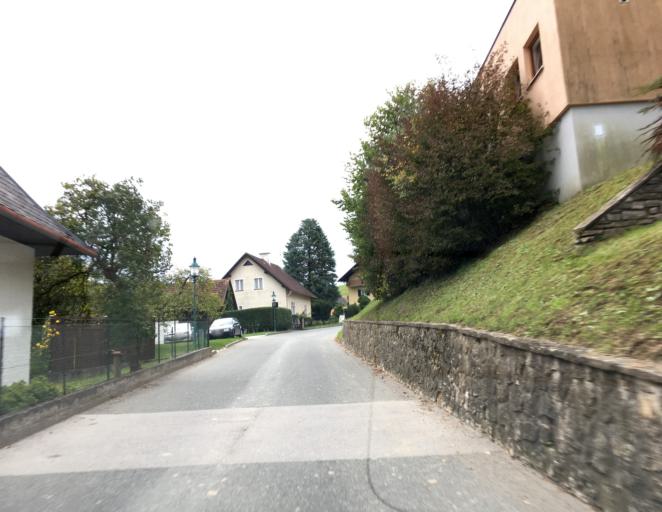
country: AT
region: Lower Austria
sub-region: Politischer Bezirk Wiener Neustadt
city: Bad Schonau
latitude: 47.4951
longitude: 16.2347
